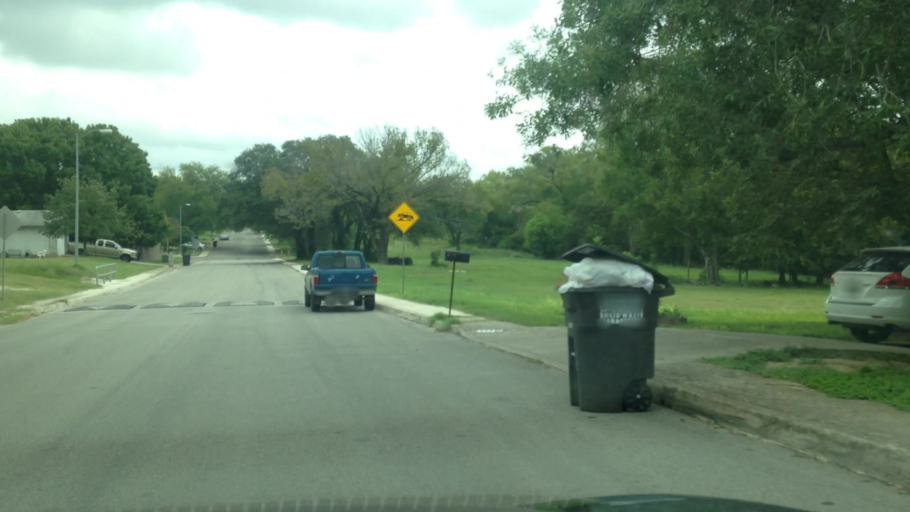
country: US
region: Texas
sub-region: Bexar County
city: Windcrest
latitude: 29.5776
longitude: -98.4069
